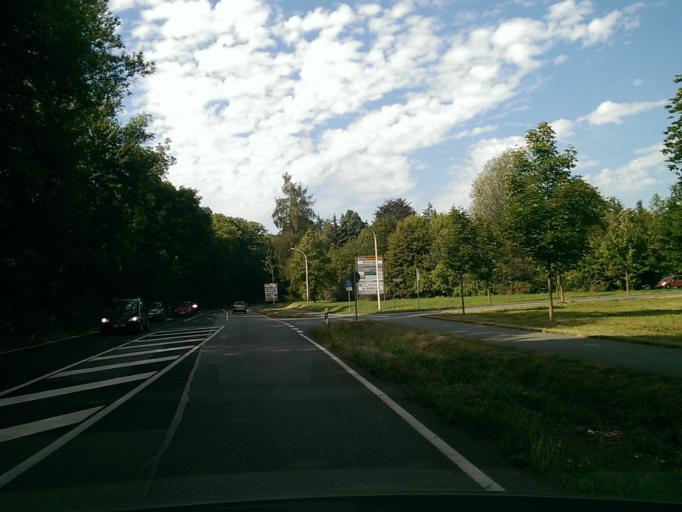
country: DE
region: Saxony
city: Zittau
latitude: 50.9051
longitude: 14.8328
